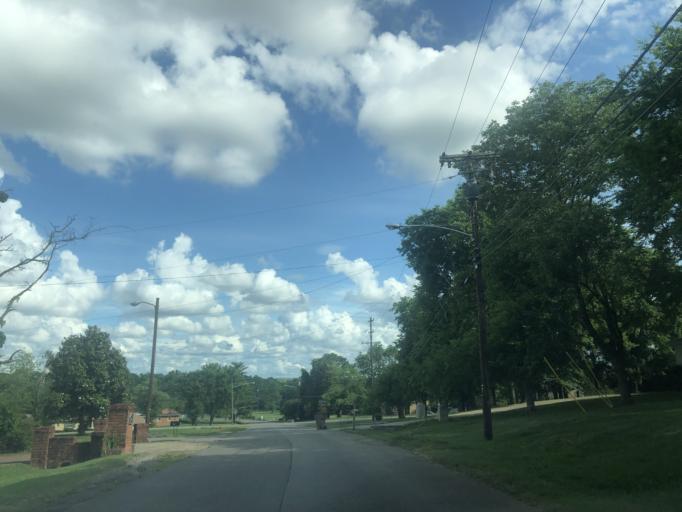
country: US
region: Tennessee
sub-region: Davidson County
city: Nashville
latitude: 36.2105
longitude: -86.8560
